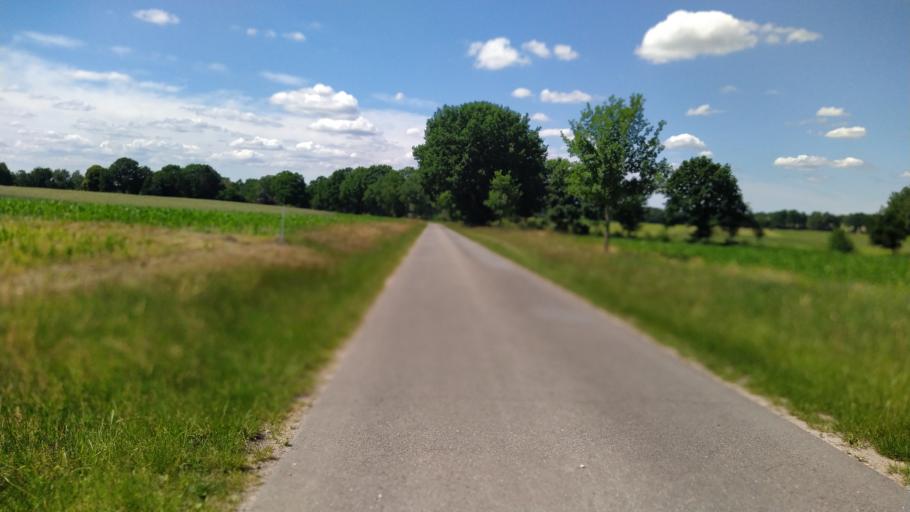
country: DE
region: Lower Saxony
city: Estorf
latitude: 53.5618
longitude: 9.2199
